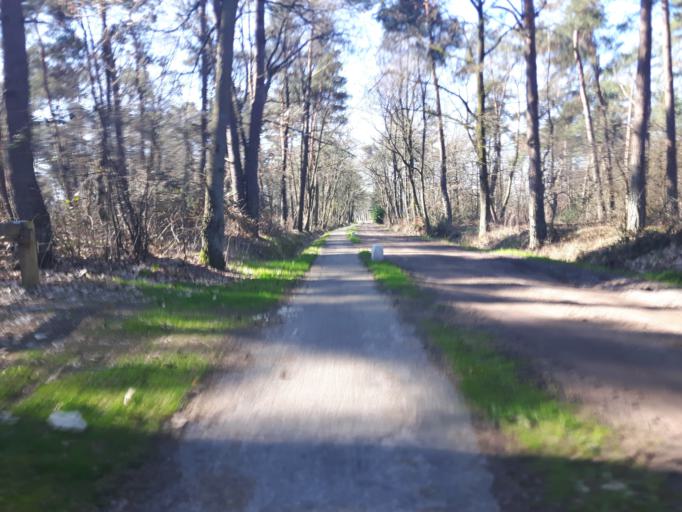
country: NL
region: Overijssel
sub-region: Gemeente Haaksbergen
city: Haaksbergen
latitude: 52.1746
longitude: 6.8181
